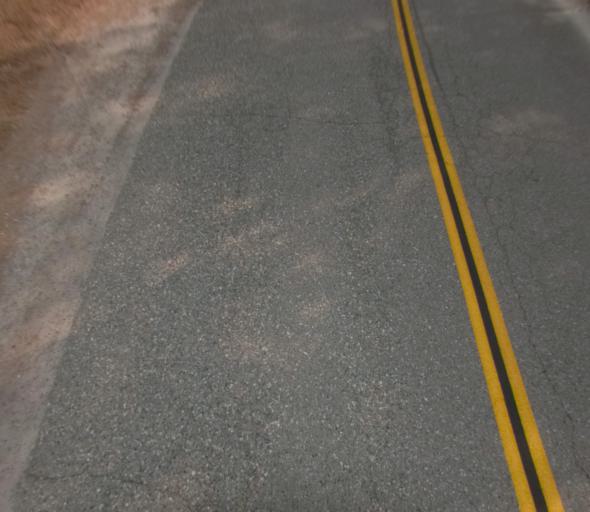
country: US
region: California
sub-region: Madera County
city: Coarsegold
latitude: 37.2032
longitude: -119.6880
